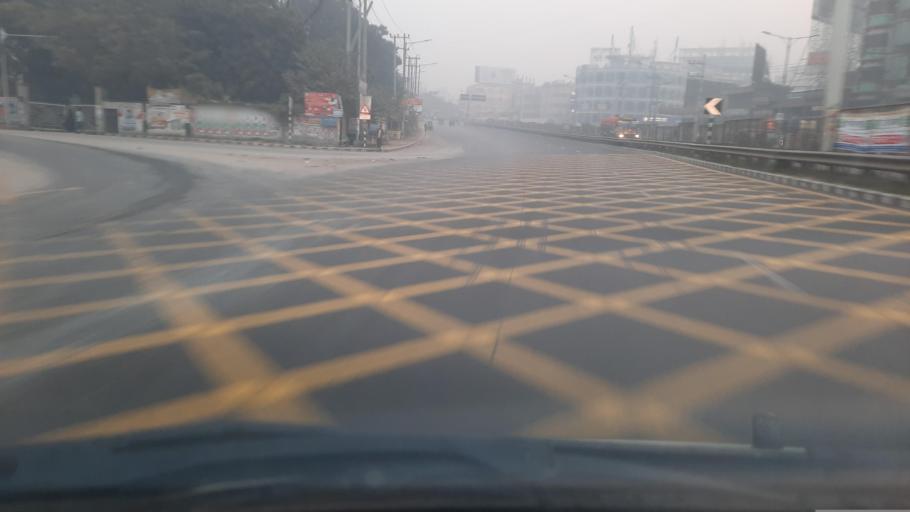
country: BD
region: Dhaka
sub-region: Dhaka
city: Dhaka
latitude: 23.6831
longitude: 90.4218
